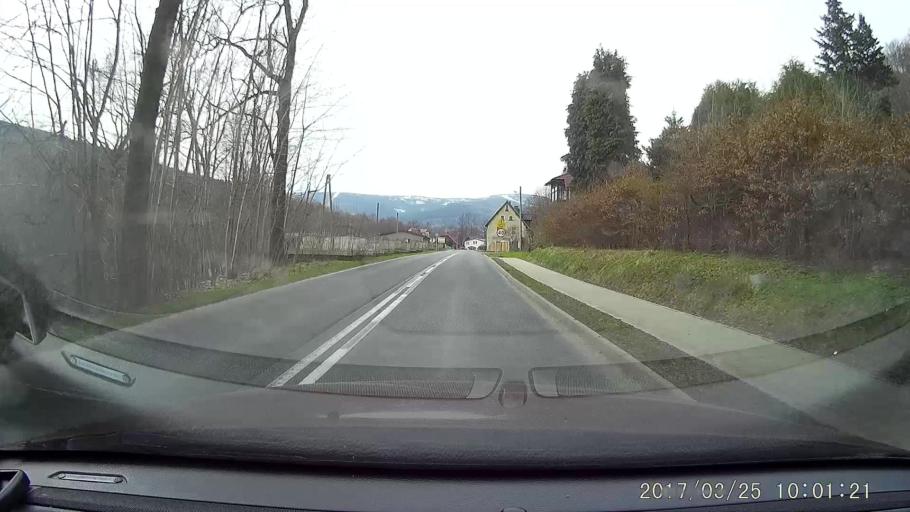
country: PL
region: Lower Silesian Voivodeship
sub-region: Powiat lubanski
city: Swieradow-Zdroj
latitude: 50.9274
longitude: 15.3531
